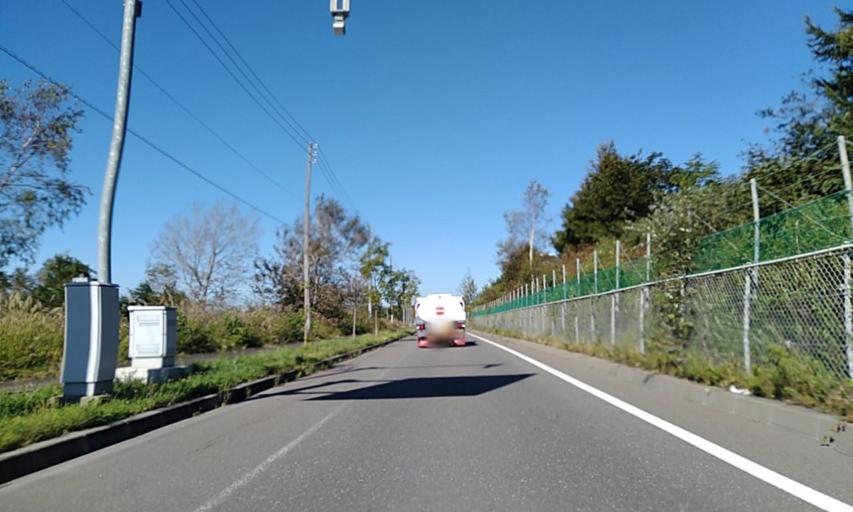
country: JP
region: Hokkaido
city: Tomakomai
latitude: 42.6920
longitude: 141.6898
